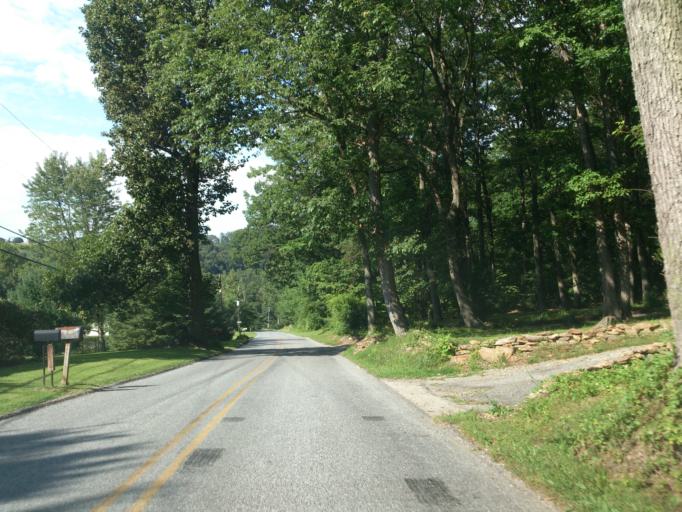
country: US
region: Pennsylvania
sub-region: York County
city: Windsor
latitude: 39.8988
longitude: -76.5343
